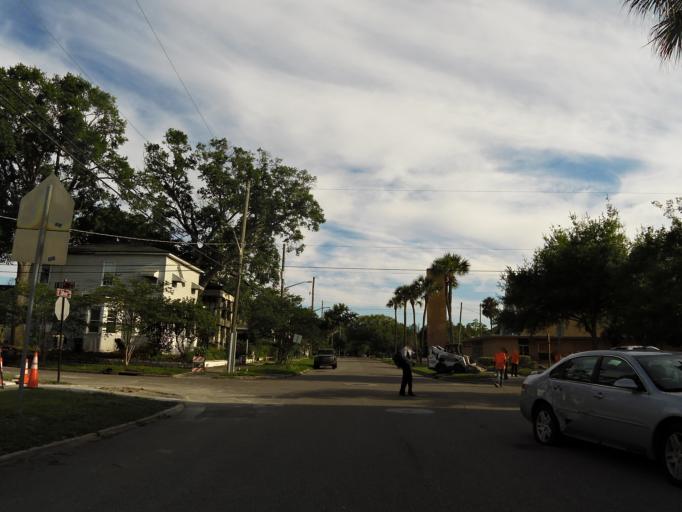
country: US
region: Florida
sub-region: Duval County
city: Jacksonville
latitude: 30.3502
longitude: -81.6568
